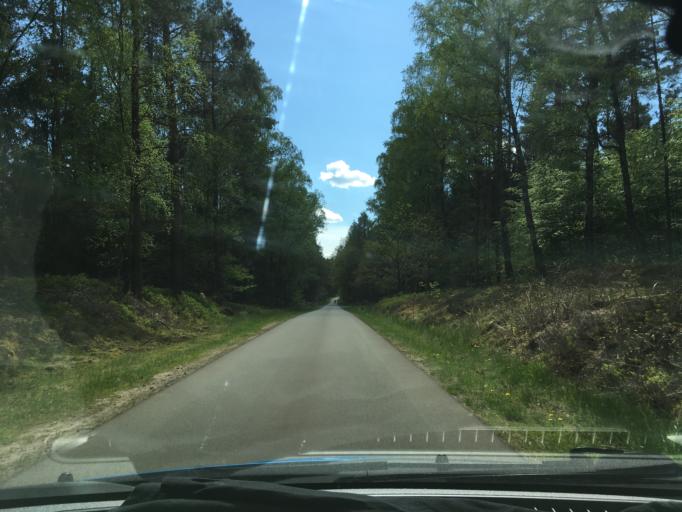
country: DE
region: Lower Saxony
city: Stoetze
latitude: 53.1140
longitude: 10.7886
